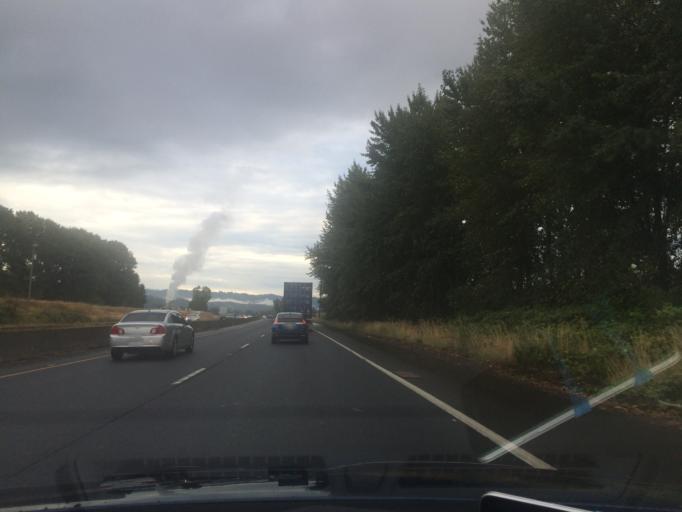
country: US
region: Washington
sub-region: Cowlitz County
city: Longview
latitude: 46.1179
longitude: -122.9182
